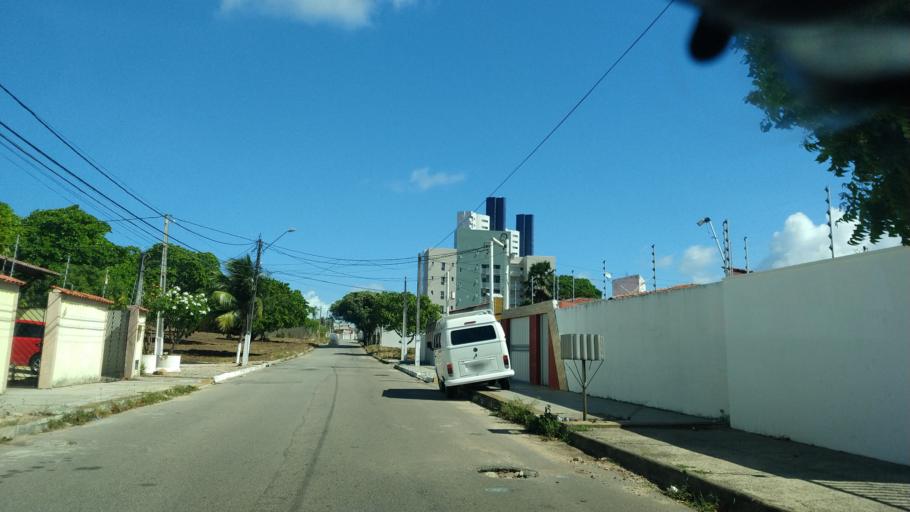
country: BR
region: Rio Grande do Norte
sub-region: Natal
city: Natal
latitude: -5.8700
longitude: -35.1922
